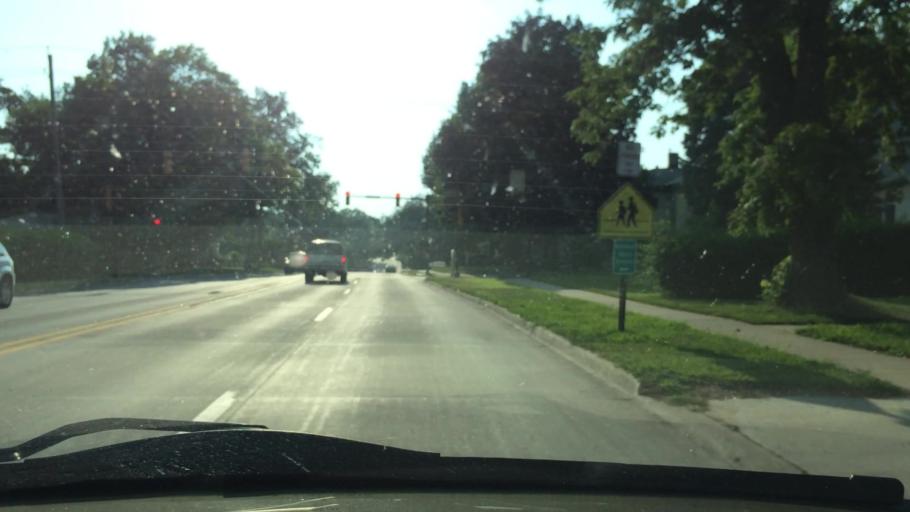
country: US
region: Iowa
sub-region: Henry County
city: Mount Pleasant
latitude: 40.9645
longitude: -91.5441
